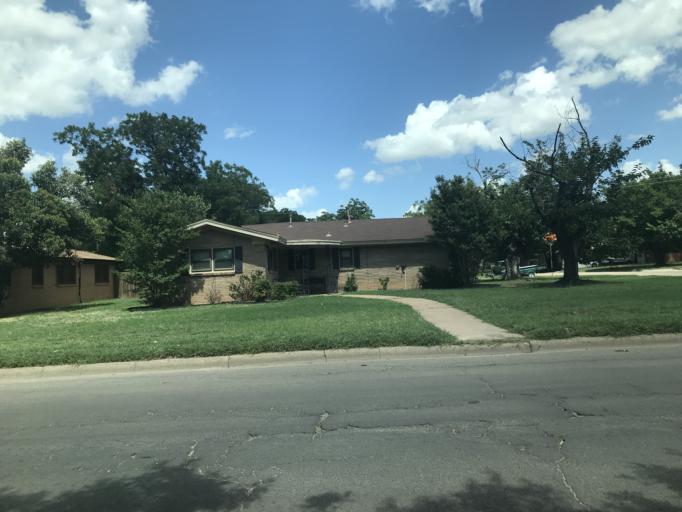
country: US
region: Texas
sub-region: Taylor County
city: Abilene
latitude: 32.4220
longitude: -99.7635
